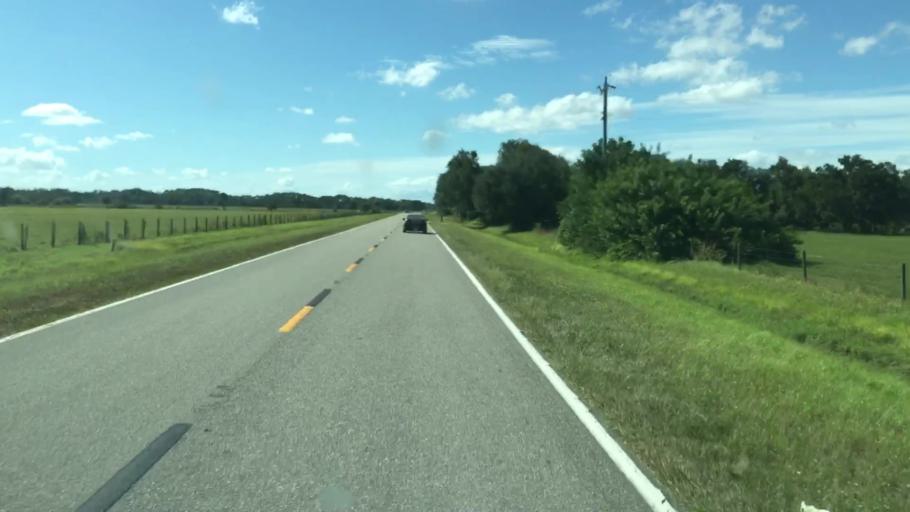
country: US
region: Florida
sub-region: Lee County
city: Fort Myers Shores
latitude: 26.7401
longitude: -81.7416
